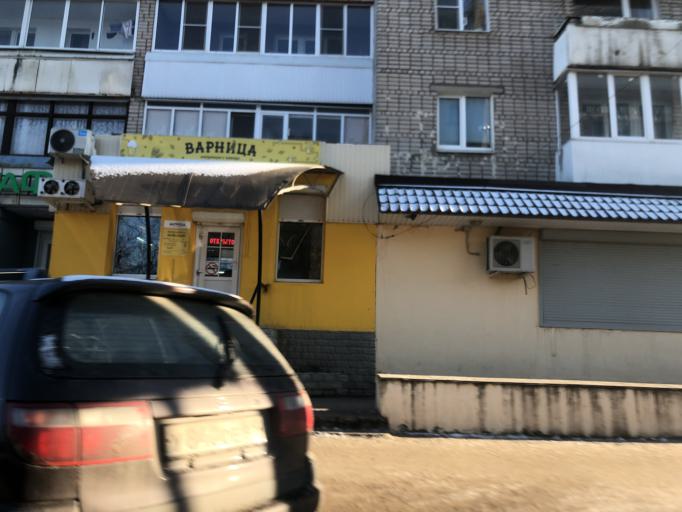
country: RU
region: Tverskaya
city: Rzhev
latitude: 56.2614
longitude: 34.3506
